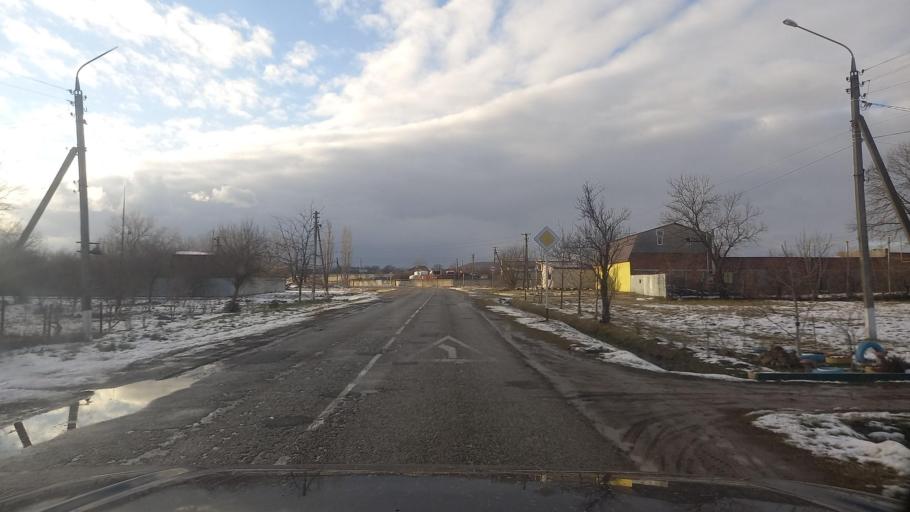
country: RU
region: Krasnodarskiy
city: Smolenskaya
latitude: 44.7767
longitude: 38.8356
